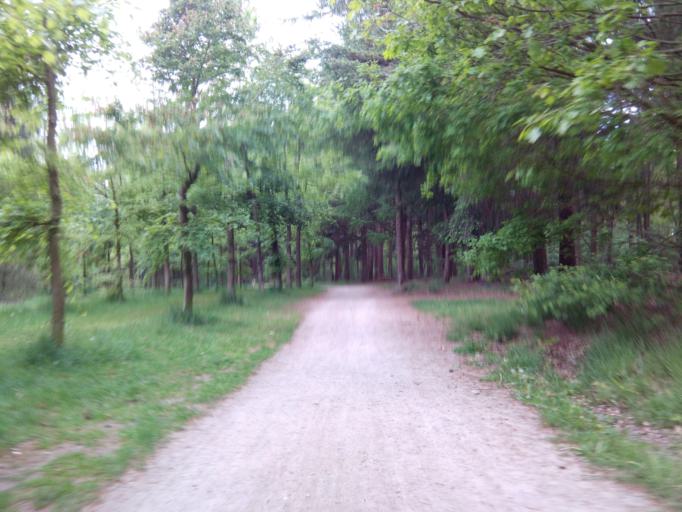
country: NL
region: Gelderland
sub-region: Gemeente Ede
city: Ede
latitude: 52.0562
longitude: 5.6572
